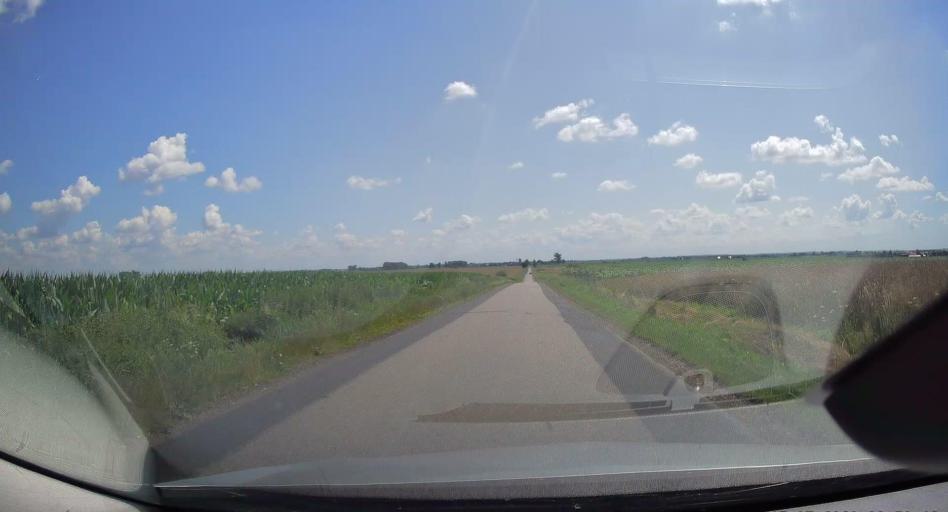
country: PL
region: Subcarpathian Voivodeship
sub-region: Powiat przemyski
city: Orly
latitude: 49.8749
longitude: 22.8223
